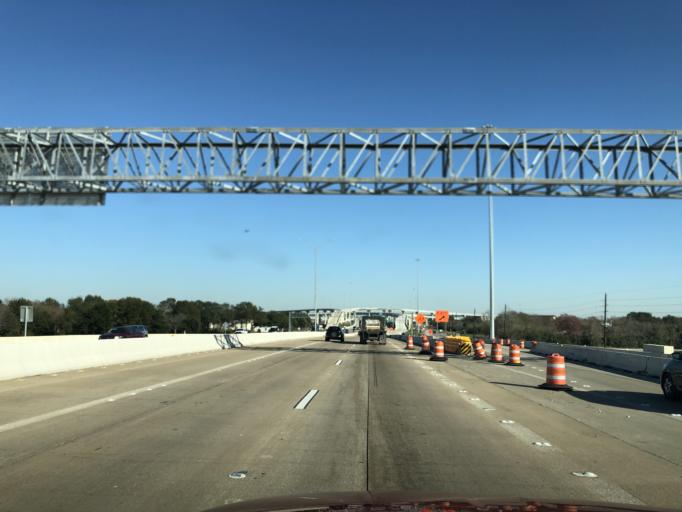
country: US
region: Texas
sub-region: Fort Bend County
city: Fresno
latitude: 29.5969
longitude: -95.3999
